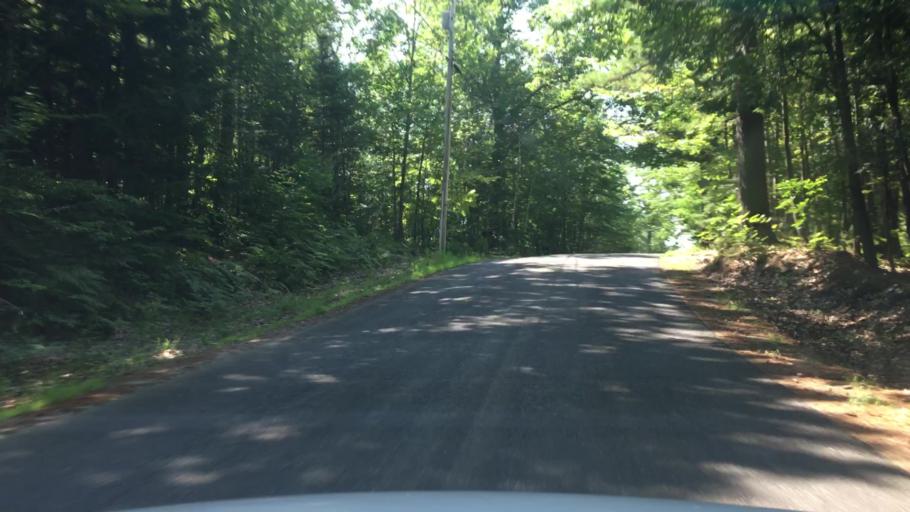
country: US
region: Maine
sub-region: Androscoggin County
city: Greene
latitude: 44.2295
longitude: -70.1049
